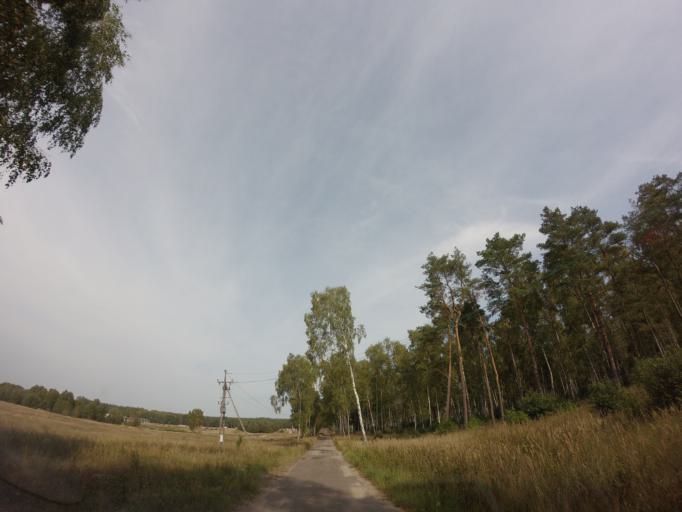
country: PL
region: West Pomeranian Voivodeship
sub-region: Powiat drawski
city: Drawsko Pomorskie
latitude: 53.4645
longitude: 15.7141
